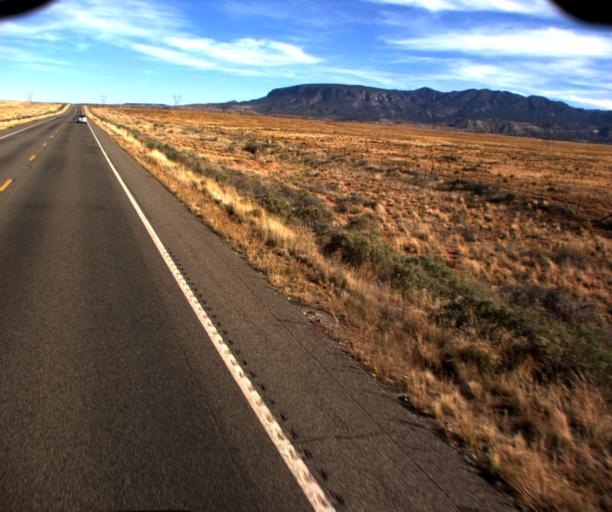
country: US
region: Arizona
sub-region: Apache County
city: Lukachukai
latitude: 36.9410
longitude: -109.2526
